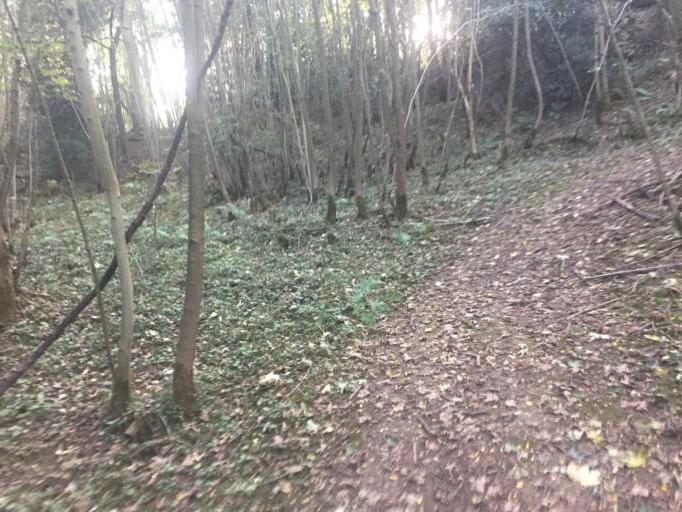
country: FR
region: Ile-de-France
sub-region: Departement des Yvelines
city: Jouy-en-Josas
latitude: 48.7574
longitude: 2.1615
